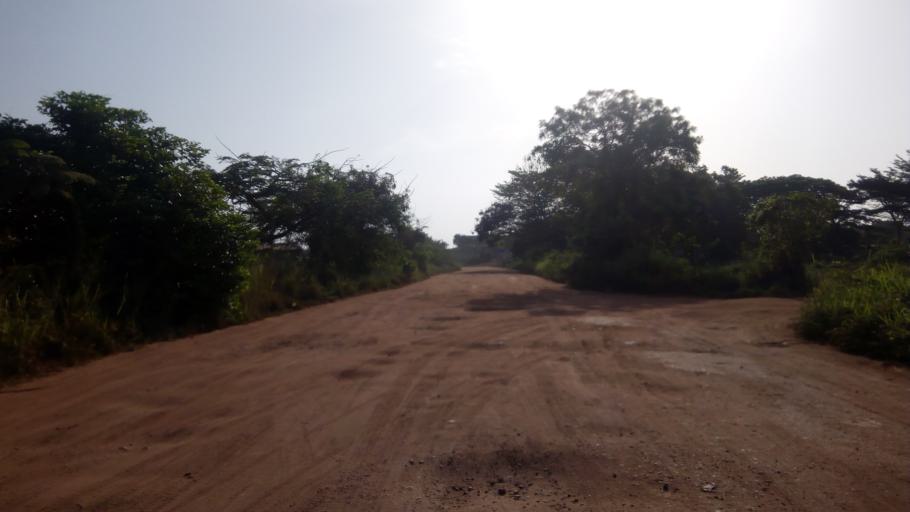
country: GH
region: Central
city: Cape Coast
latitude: 5.1151
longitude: -1.2760
